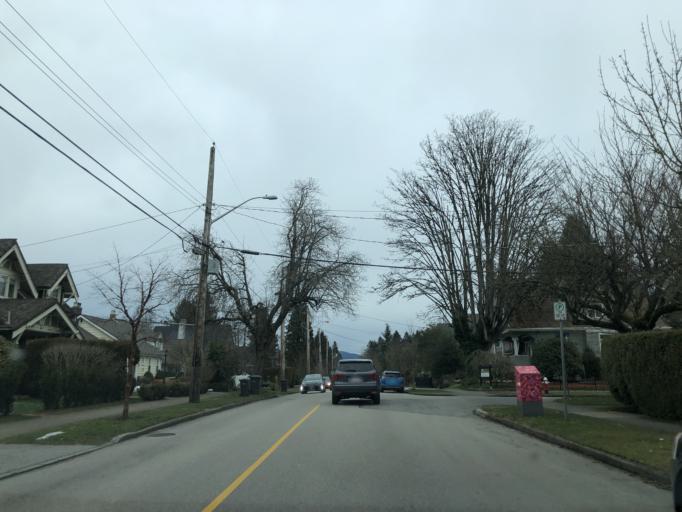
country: CA
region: British Columbia
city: New Westminster
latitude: 49.2150
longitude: -122.9167
